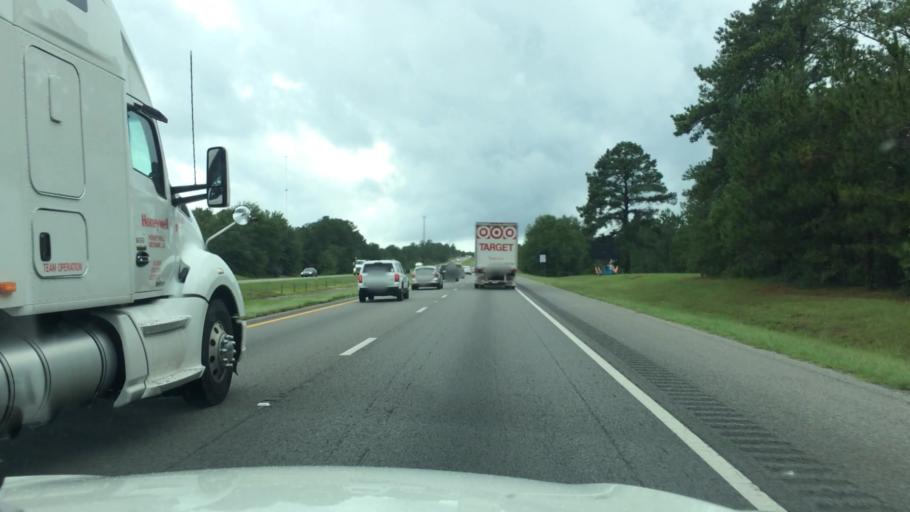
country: US
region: South Carolina
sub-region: Kershaw County
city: Lugoff
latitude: 34.1793
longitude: -80.7021
